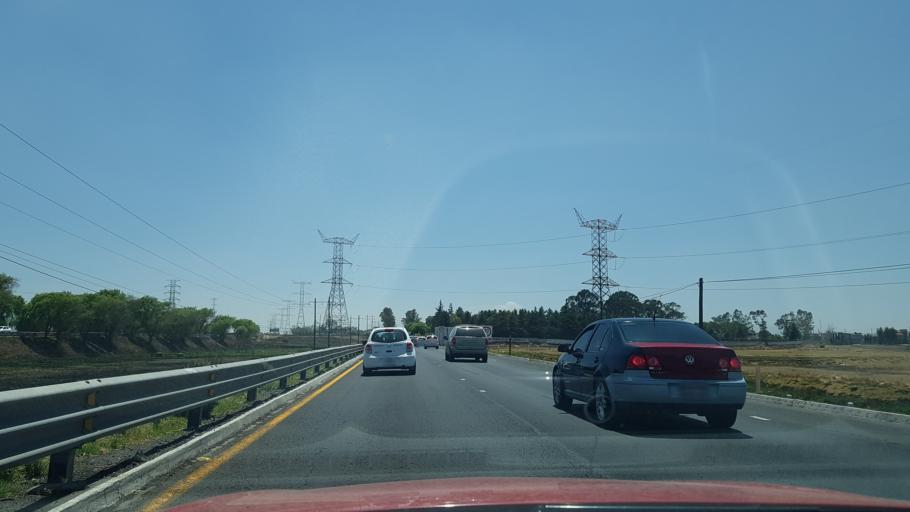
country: MX
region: Mexico
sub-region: Ixtlahuaca
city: Santo Domingo de Guzman
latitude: 19.6039
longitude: -99.7741
